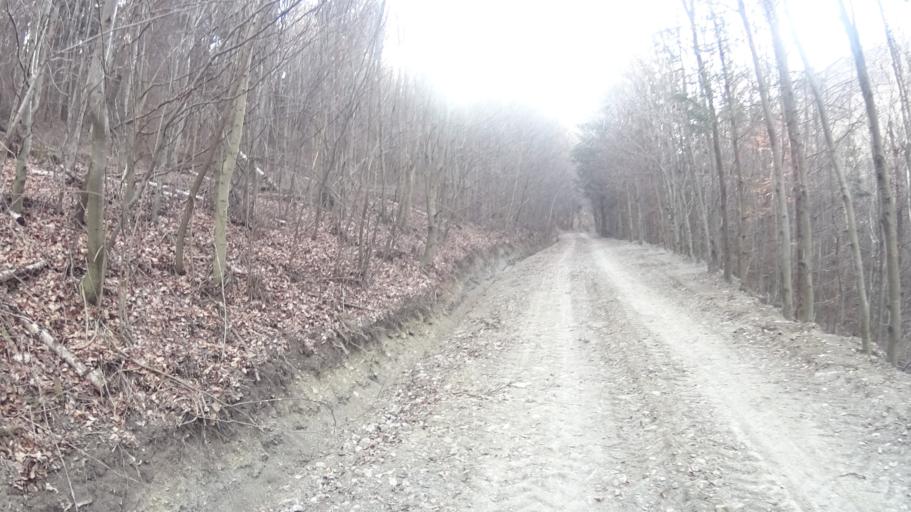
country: HU
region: Heves
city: Szilvasvarad
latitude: 48.0649
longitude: 20.4057
